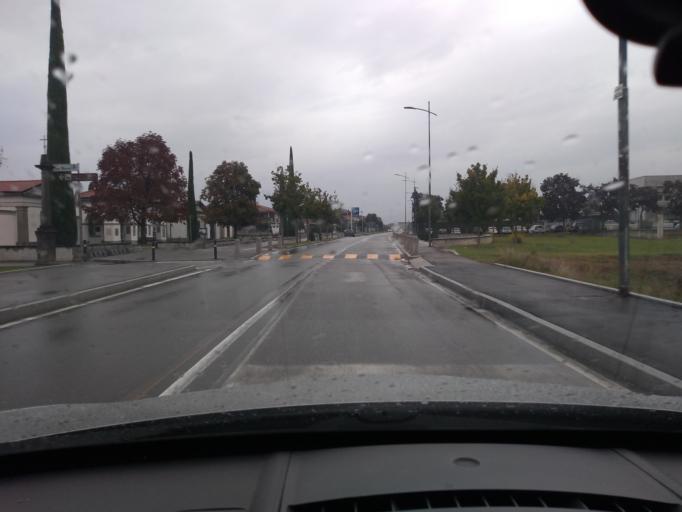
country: IT
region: Lombardy
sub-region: Provincia di Bergamo
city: Mornico al Serio
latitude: 45.5976
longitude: 9.8087
